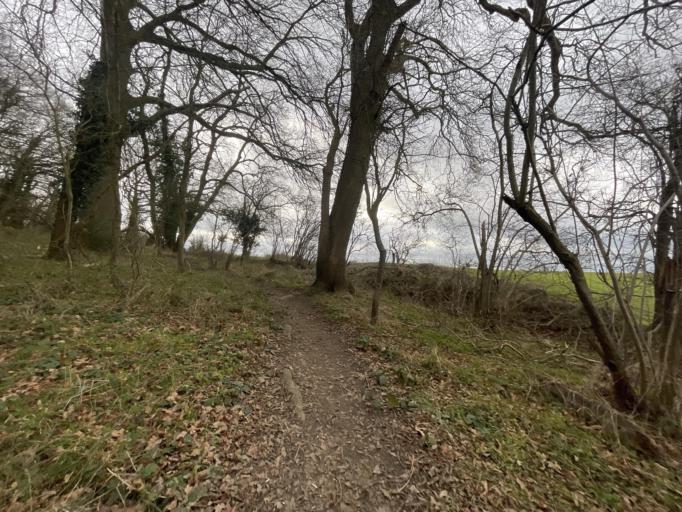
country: GB
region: England
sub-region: West Berkshire
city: Theale
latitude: 51.4486
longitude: -1.0659
